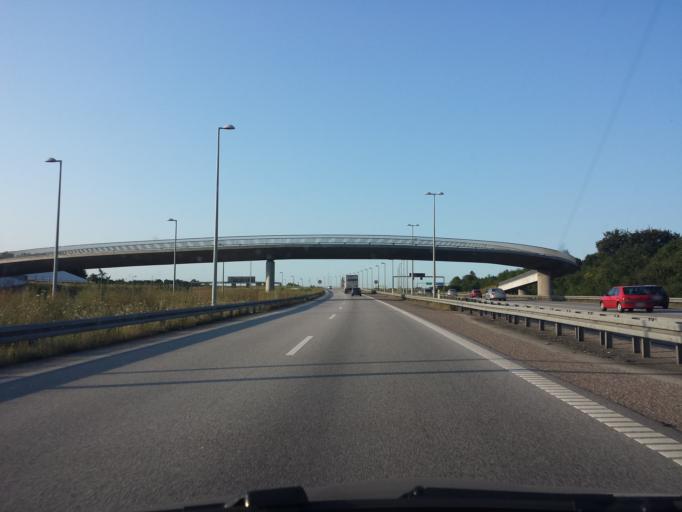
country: DK
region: Capital Region
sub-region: Rodovre Kommune
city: Rodovre
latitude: 55.6844
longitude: 12.4296
